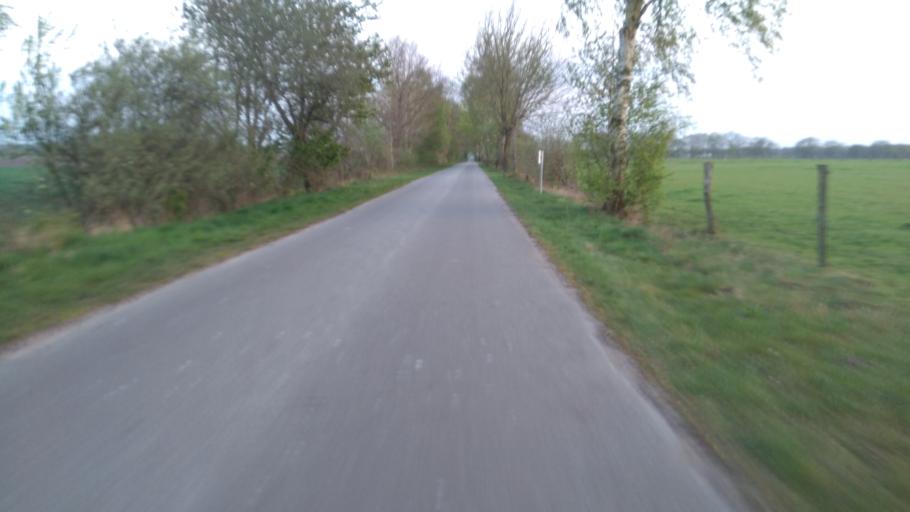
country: DE
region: Lower Saxony
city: Bargstedt
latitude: 53.4855
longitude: 9.4788
